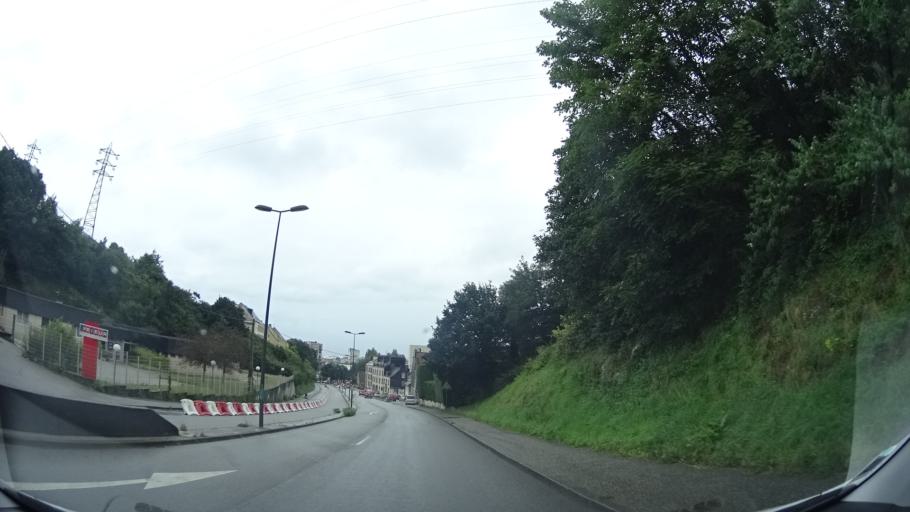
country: FR
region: Lower Normandy
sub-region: Departement de la Manche
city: Cherbourg-Octeville
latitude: 49.6300
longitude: -1.6249
